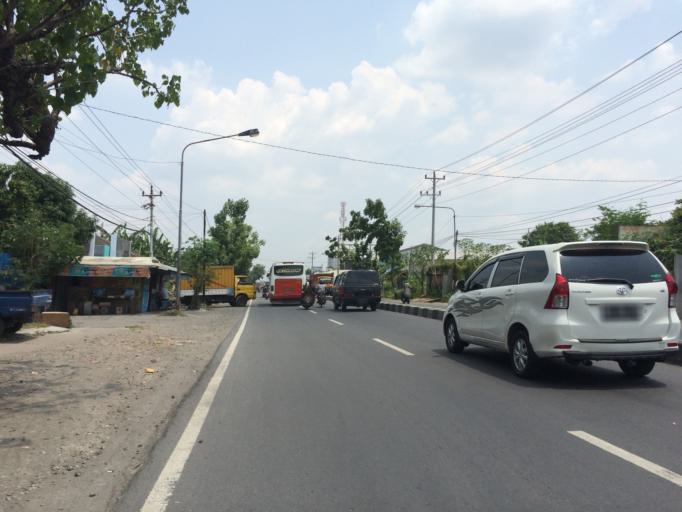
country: ID
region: Central Java
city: Grogol
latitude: -7.6228
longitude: 110.8221
